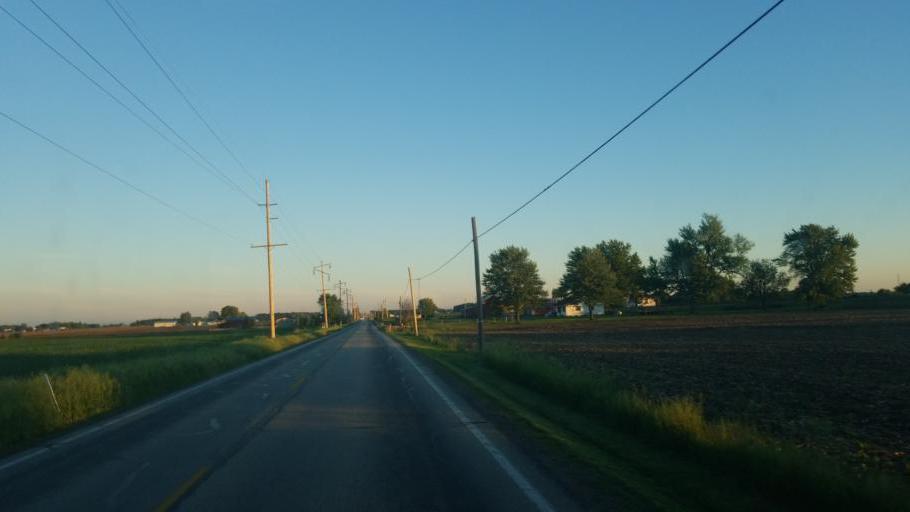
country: US
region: Indiana
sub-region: Elkhart County
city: Nappanee
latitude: 41.4222
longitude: -86.0013
